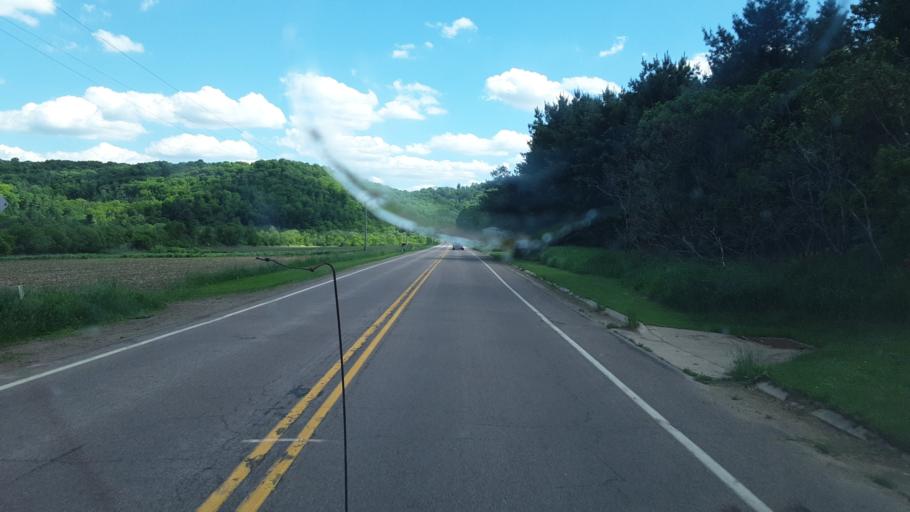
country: US
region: Wisconsin
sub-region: Richland County
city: Richland Center
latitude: 43.4011
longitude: -90.2432
